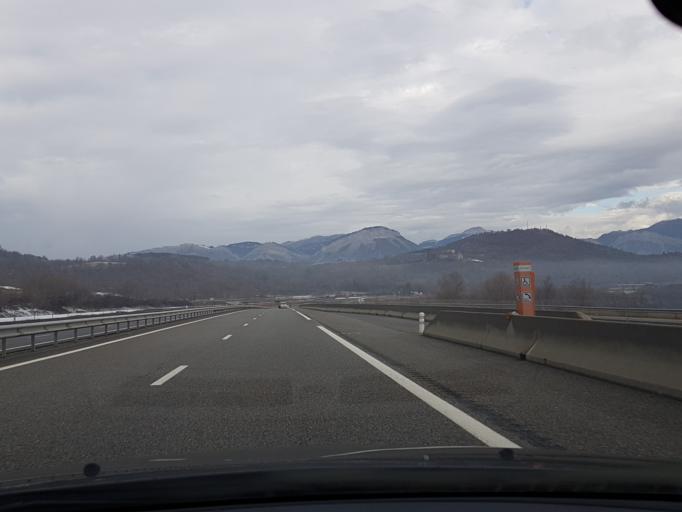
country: FR
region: Provence-Alpes-Cote d'Azur
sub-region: Departement des Hautes-Alpes
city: Laragne-Monteglin
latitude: 44.3166
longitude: 5.8946
